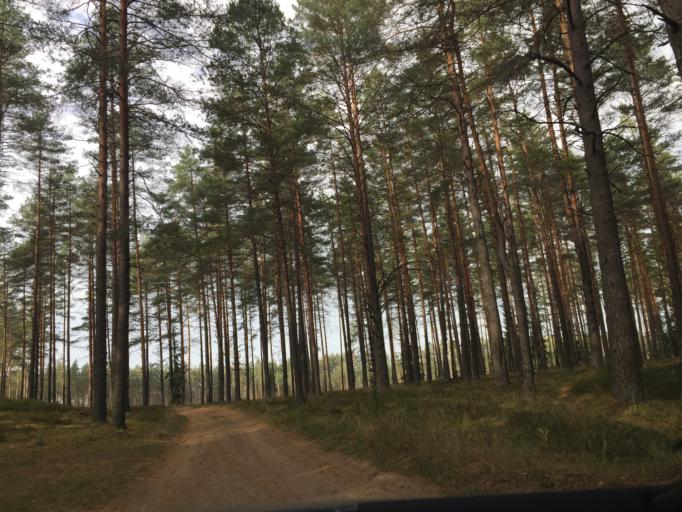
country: LV
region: Garkalne
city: Garkalne
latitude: 56.9530
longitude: 24.4246
